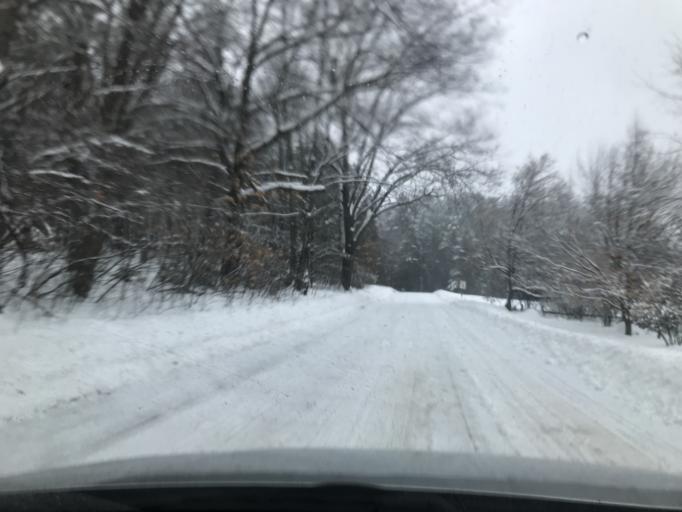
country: US
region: Wisconsin
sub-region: Marinette County
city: Peshtigo
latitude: 45.3815
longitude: -87.9539
